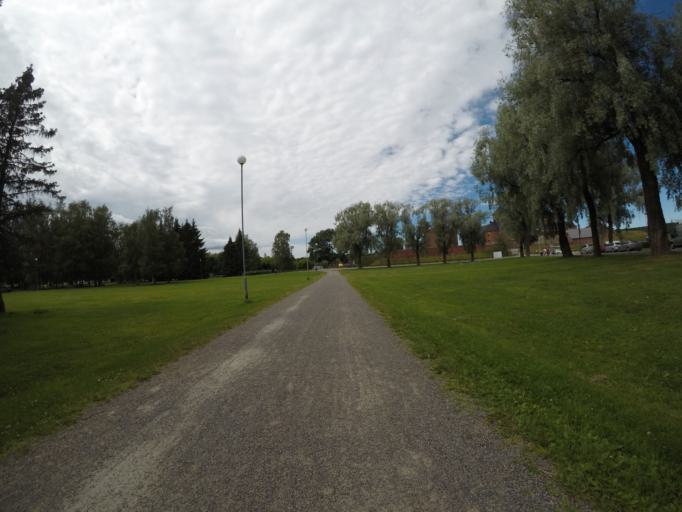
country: FI
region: Haeme
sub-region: Haemeenlinna
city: Haemeenlinna
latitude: 61.0015
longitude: 24.4609
